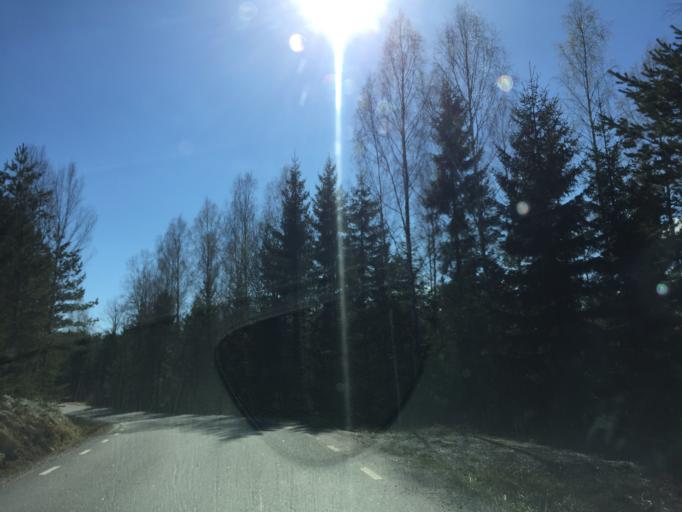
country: SE
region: OErebro
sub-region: Orebro Kommun
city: Hovsta
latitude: 59.3547
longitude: 15.1305
